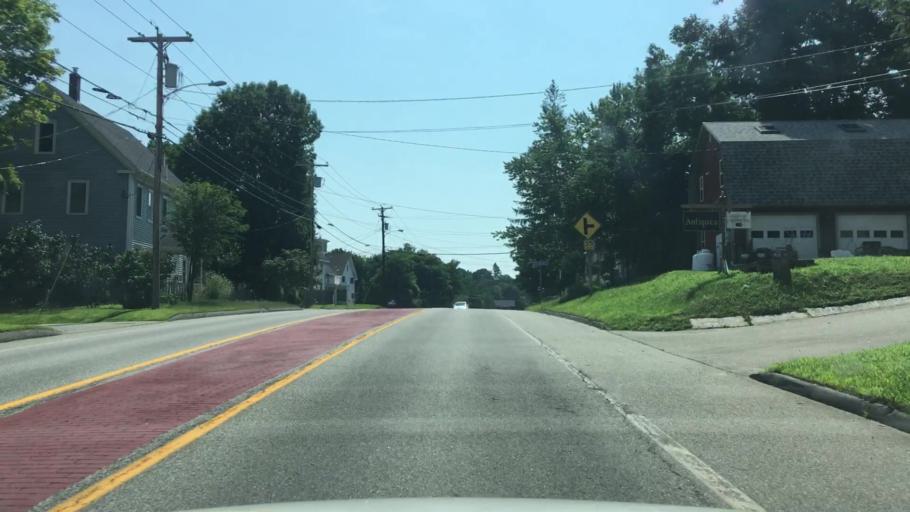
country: US
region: Maine
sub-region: Kennebec County
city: Hallowell
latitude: 44.2687
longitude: -69.7885
